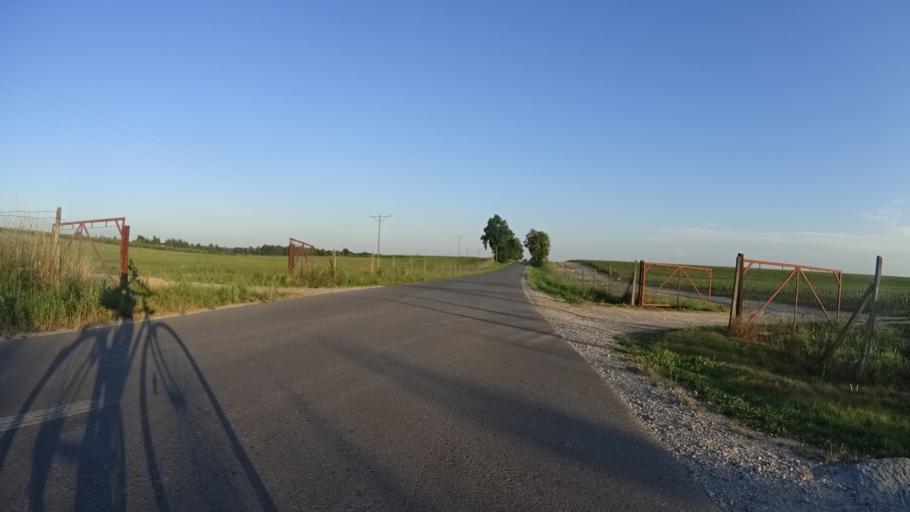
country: PL
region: Masovian Voivodeship
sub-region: Powiat grojecki
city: Goszczyn
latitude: 51.6840
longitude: 20.8236
